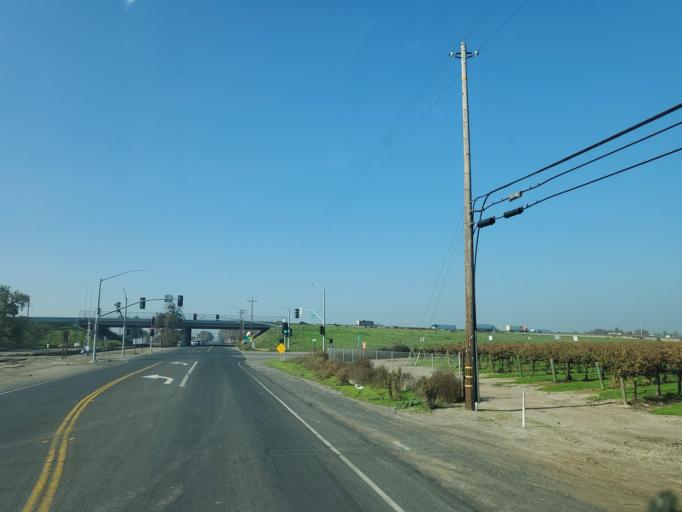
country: US
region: California
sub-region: San Joaquin County
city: French Camp
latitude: 37.8592
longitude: -121.2162
